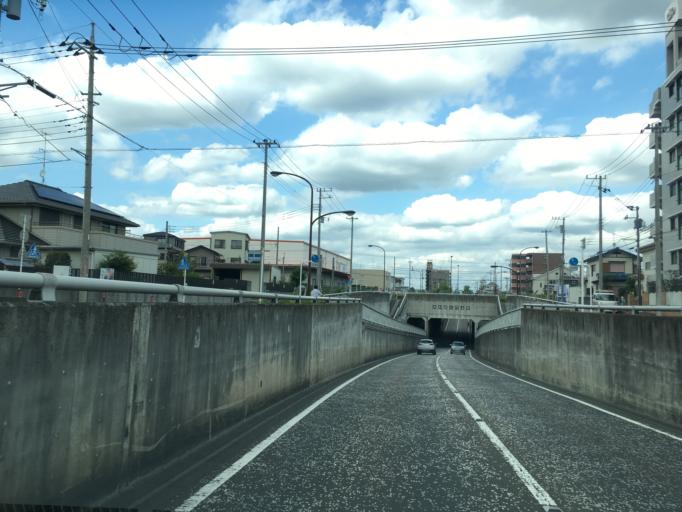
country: JP
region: Tokyo
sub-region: Machida-shi
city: Machida
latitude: 35.5618
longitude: 139.4056
